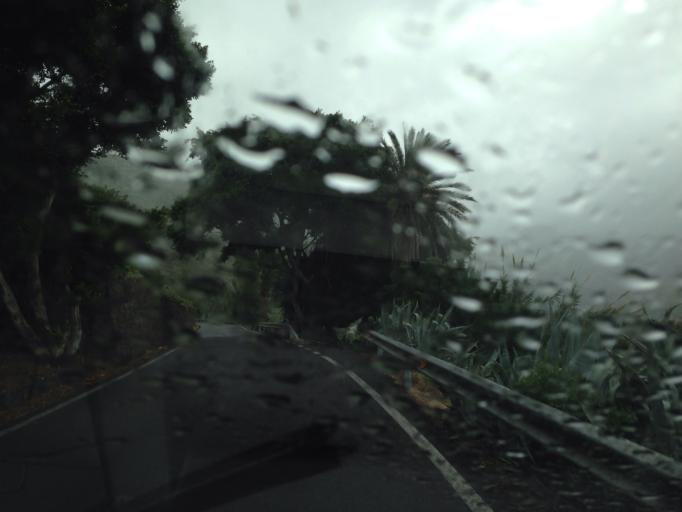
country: ES
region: Canary Islands
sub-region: Provincia de Las Palmas
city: Agaete
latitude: 28.0959
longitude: -15.6876
